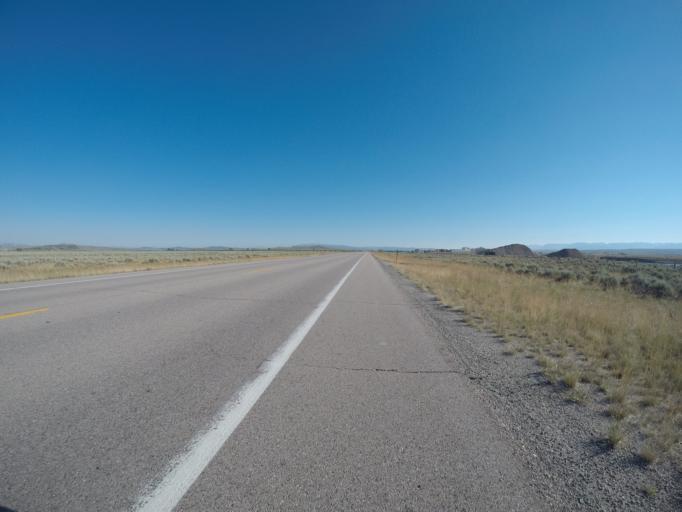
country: US
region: Wyoming
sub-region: Sublette County
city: Pinedale
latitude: 42.9681
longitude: -110.0892
